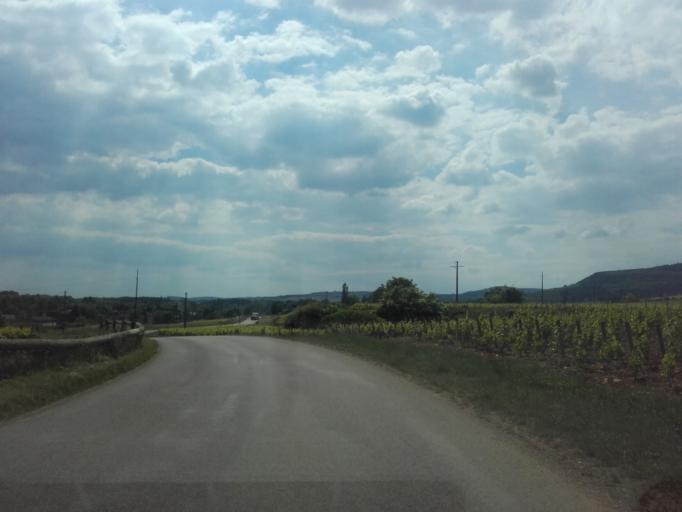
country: FR
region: Bourgogne
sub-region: Departement de Saone-et-Loire
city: Chagny
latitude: 46.9140
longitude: 4.7091
